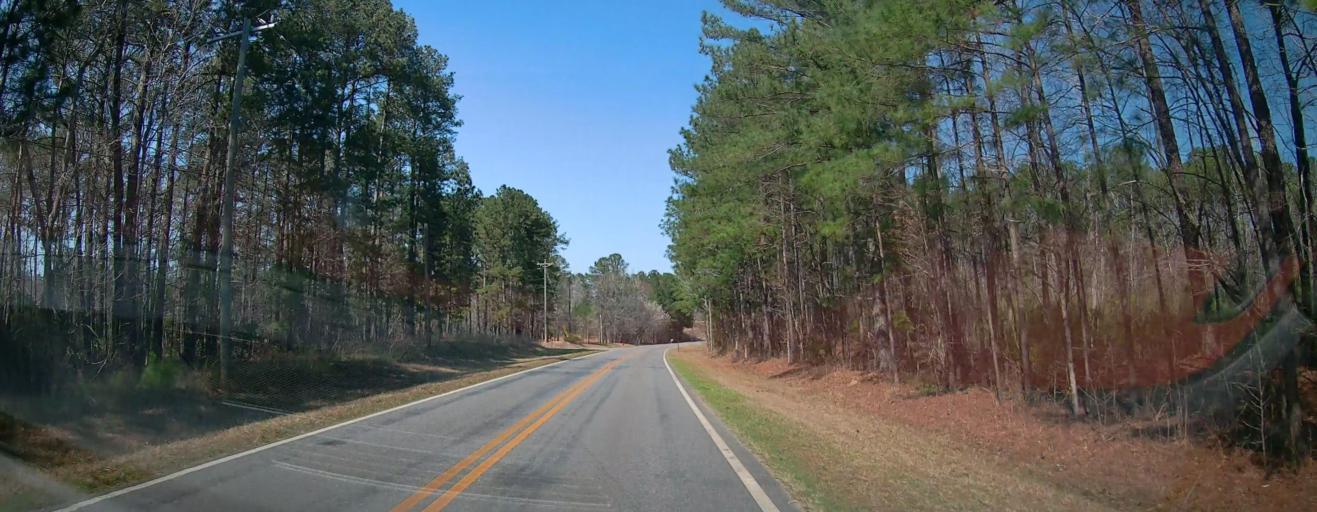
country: US
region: Georgia
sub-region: Jones County
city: Gray
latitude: 32.9707
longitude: -83.5479
